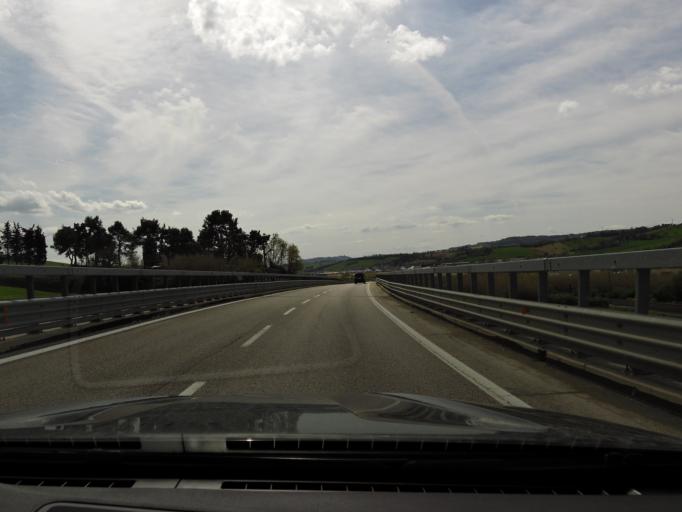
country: IT
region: The Marches
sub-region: Provincia di Ancona
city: Ancona
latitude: 43.5593
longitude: 13.5190
